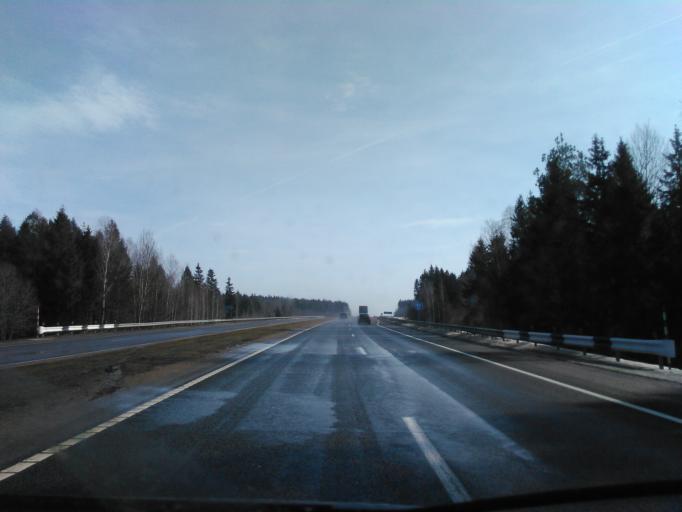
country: BY
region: Vitebsk
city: Kokhanava
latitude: 54.4787
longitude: 29.8432
